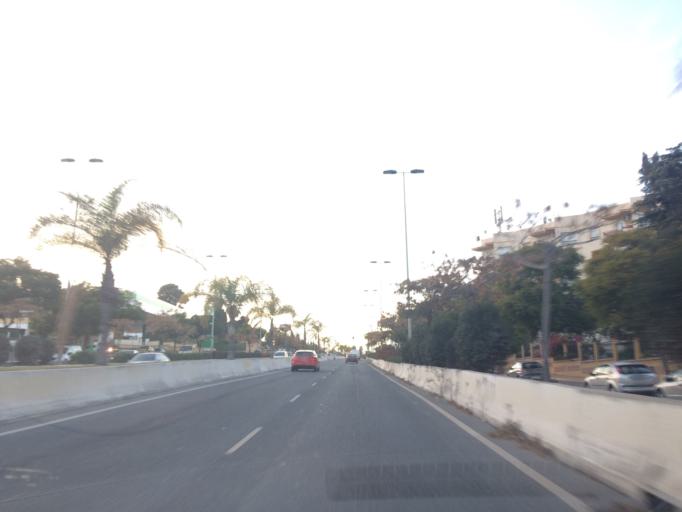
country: ES
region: Andalusia
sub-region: Provincia de Malaga
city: Torremolinos
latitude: 36.6610
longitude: -4.5010
